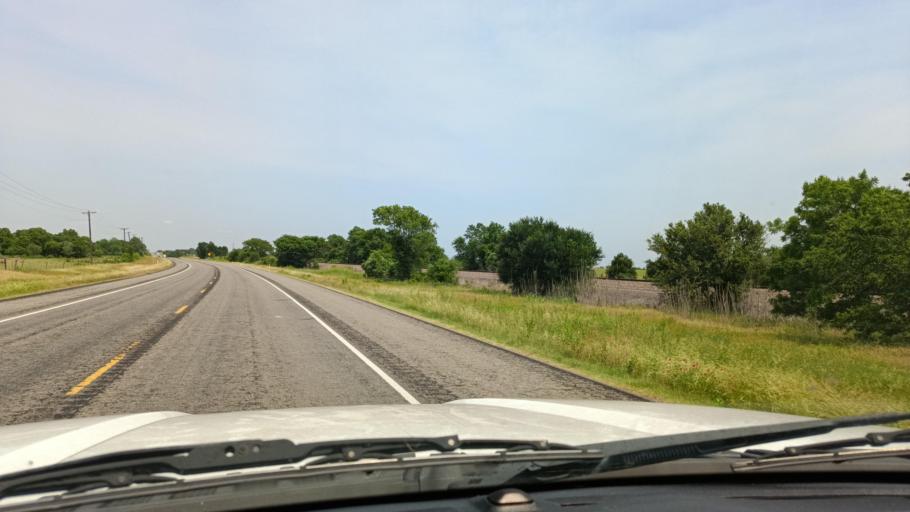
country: US
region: Texas
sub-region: Milam County
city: Cameron
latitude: 30.8489
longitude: -97.0760
